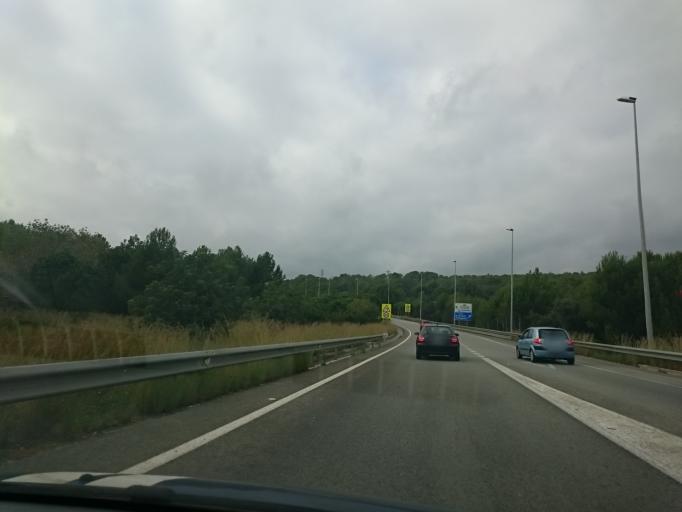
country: ES
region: Catalonia
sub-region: Provincia de Barcelona
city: Sant Pere de Ribes
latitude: 41.2429
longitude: 1.7628
